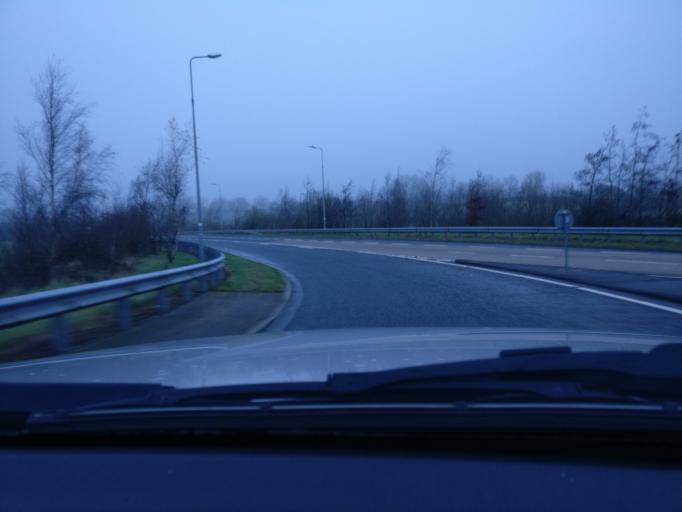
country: IE
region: Leinster
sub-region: An Iarmhi
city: Rochfortbridge
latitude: 53.3888
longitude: -7.3634
